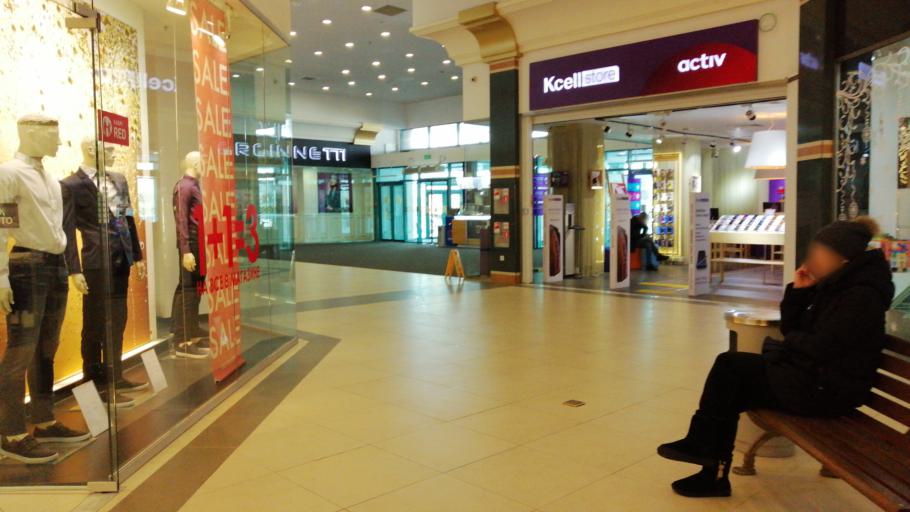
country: KZ
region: Aqtoebe
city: Aqtobe
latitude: 50.2894
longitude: 57.1937
